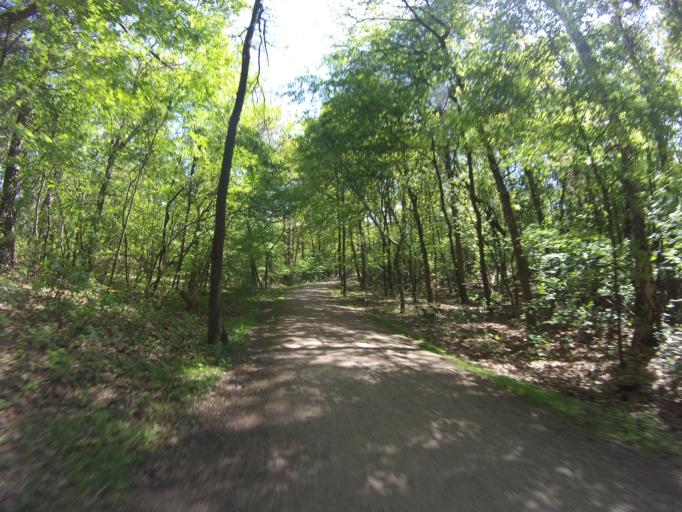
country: NL
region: North Holland
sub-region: Gemeente Hilversum
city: Hilversum
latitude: 52.2022
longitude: 5.1819
